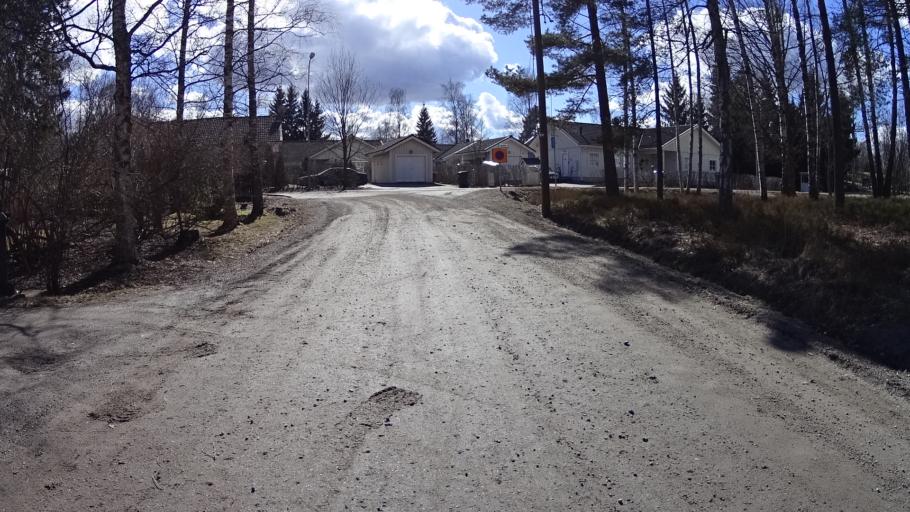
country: FI
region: Uusimaa
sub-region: Helsinki
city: Kauniainen
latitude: 60.2262
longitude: 24.7046
